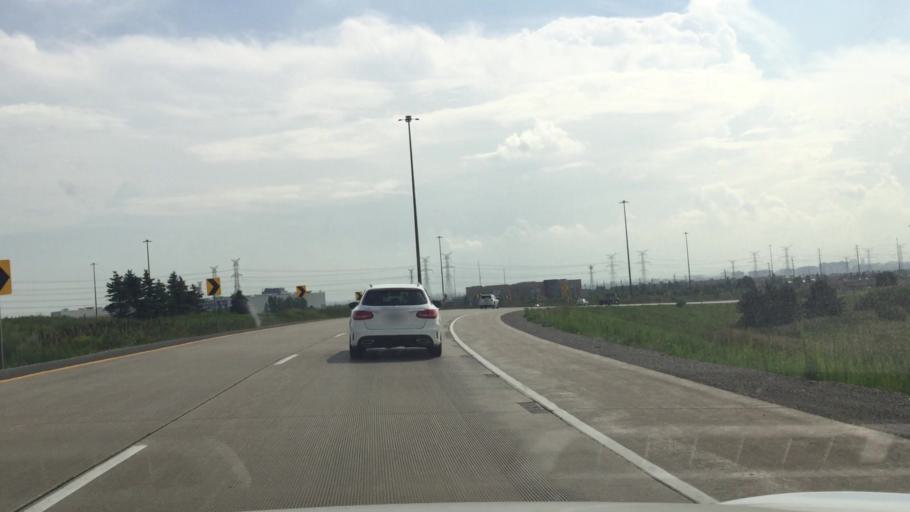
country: CA
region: Ontario
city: Concord
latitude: 43.7845
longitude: -79.5421
